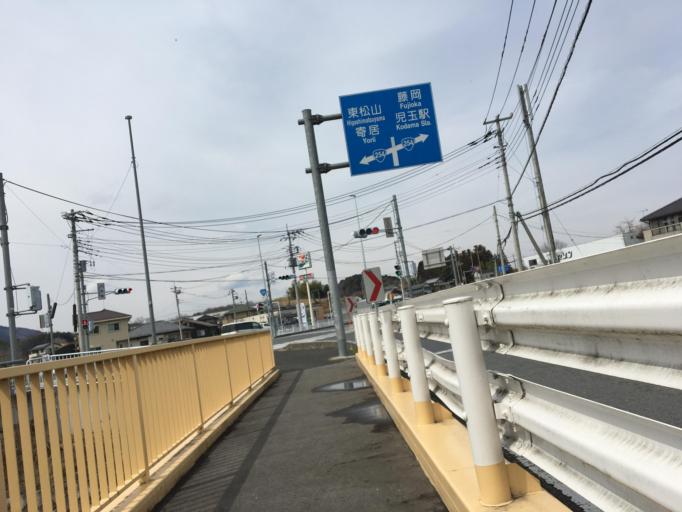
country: JP
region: Saitama
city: Yorii
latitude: 36.1592
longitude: 139.1814
